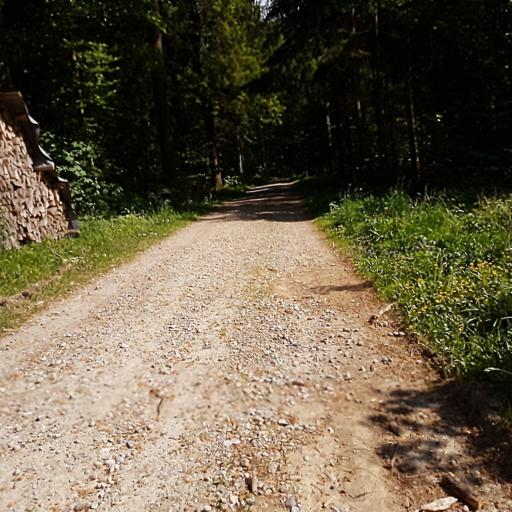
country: CH
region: Thurgau
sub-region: Arbon District
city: Amriswil
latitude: 47.5745
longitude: 9.3057
